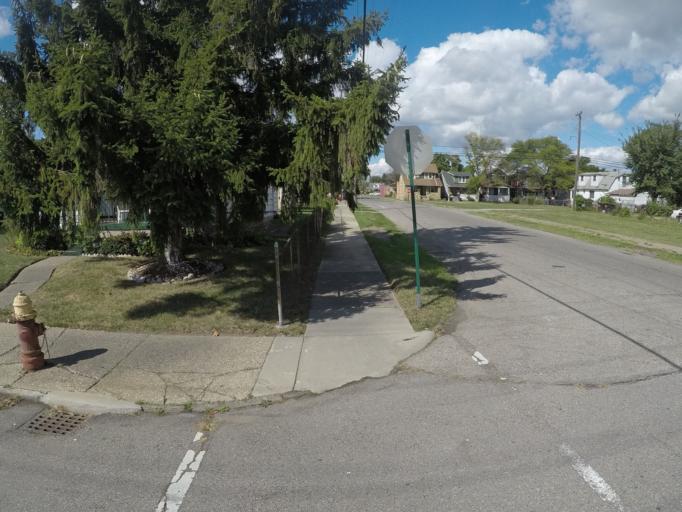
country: US
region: Michigan
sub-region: Wayne County
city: Melvindale
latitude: 42.2657
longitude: -83.1616
